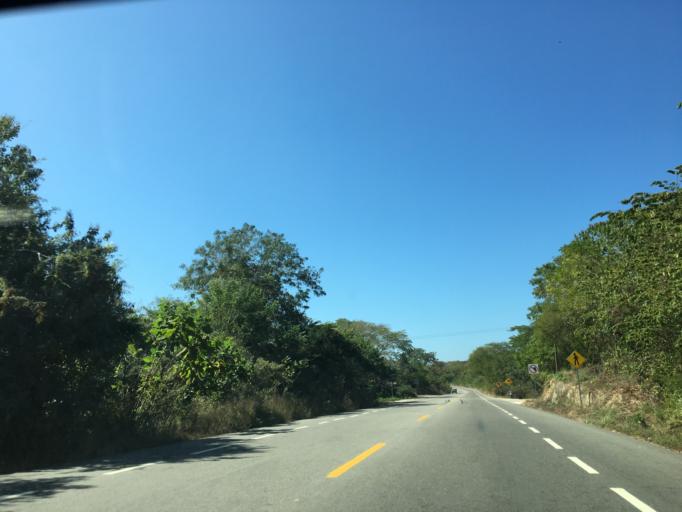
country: MX
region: Oaxaca
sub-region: Santa Maria Huatulco
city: Sector H Tres
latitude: 15.7836
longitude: -96.1920
